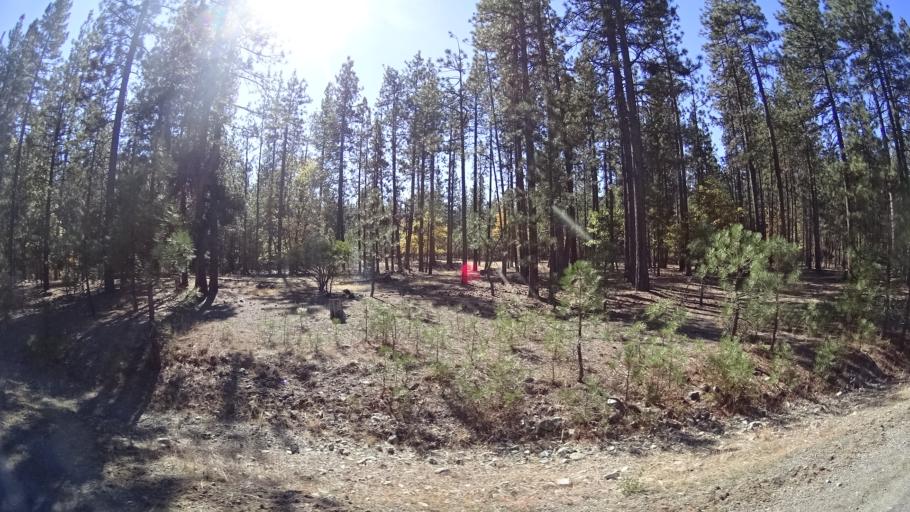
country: US
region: California
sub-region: Siskiyou County
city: Yreka
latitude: 41.5123
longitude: -122.9131
